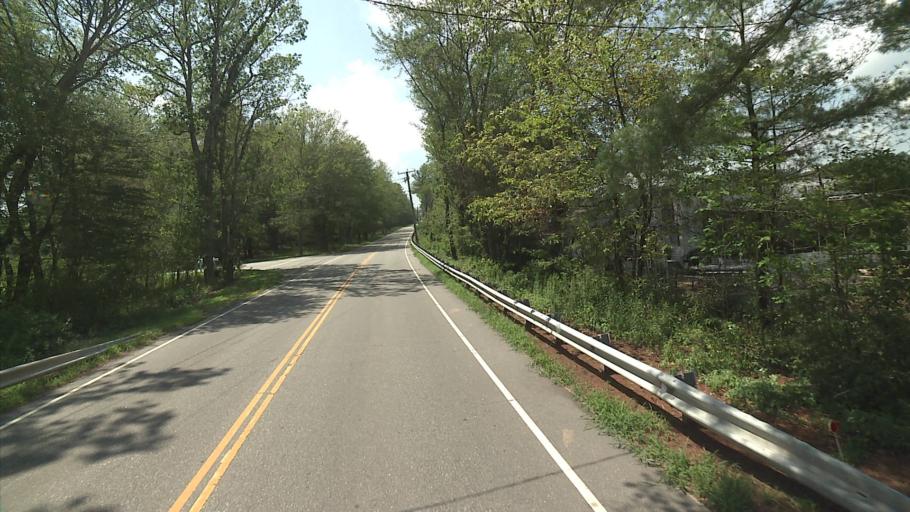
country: US
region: Connecticut
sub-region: New London County
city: Preston City
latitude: 41.5486
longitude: -71.8977
